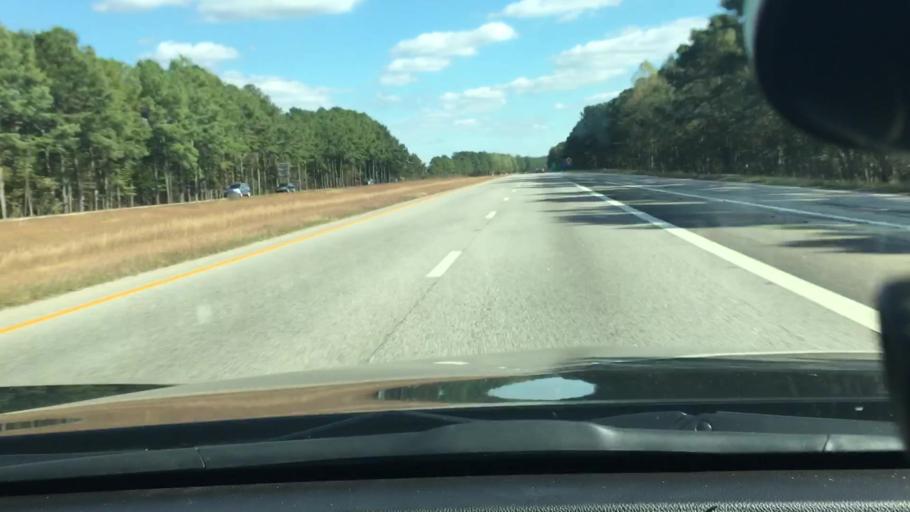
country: US
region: North Carolina
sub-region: Wilson County
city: Lucama
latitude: 35.7732
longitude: -78.0540
